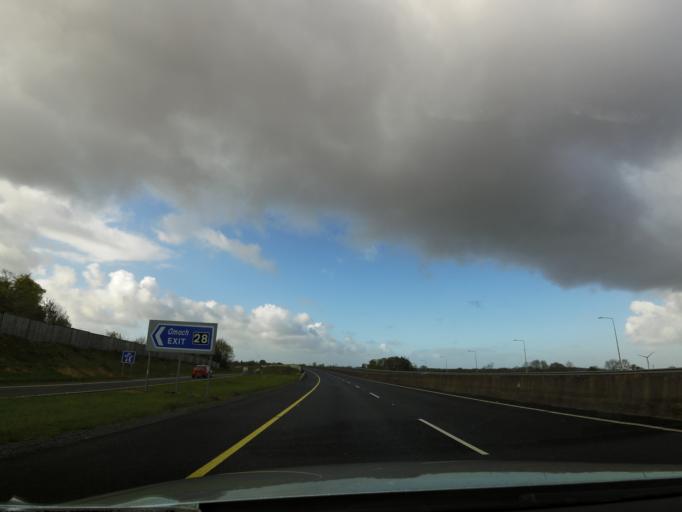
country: IE
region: Munster
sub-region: County Limerick
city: Annacotty
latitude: 52.6776
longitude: -8.5127
